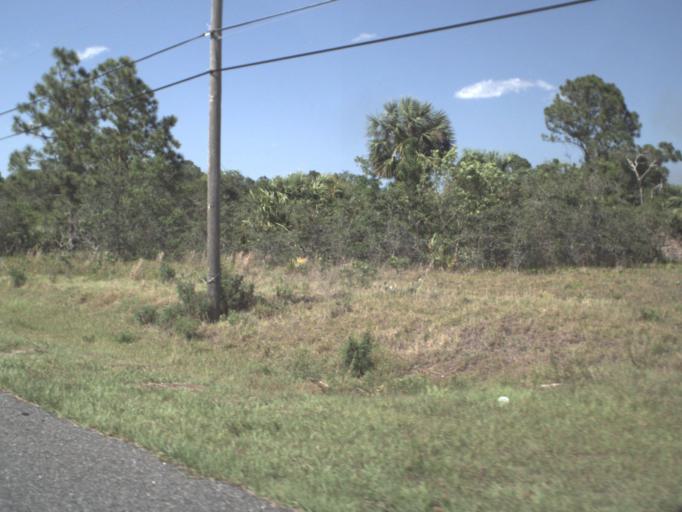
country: US
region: Florida
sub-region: Volusia County
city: Oak Hill
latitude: 28.7685
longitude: -80.8781
